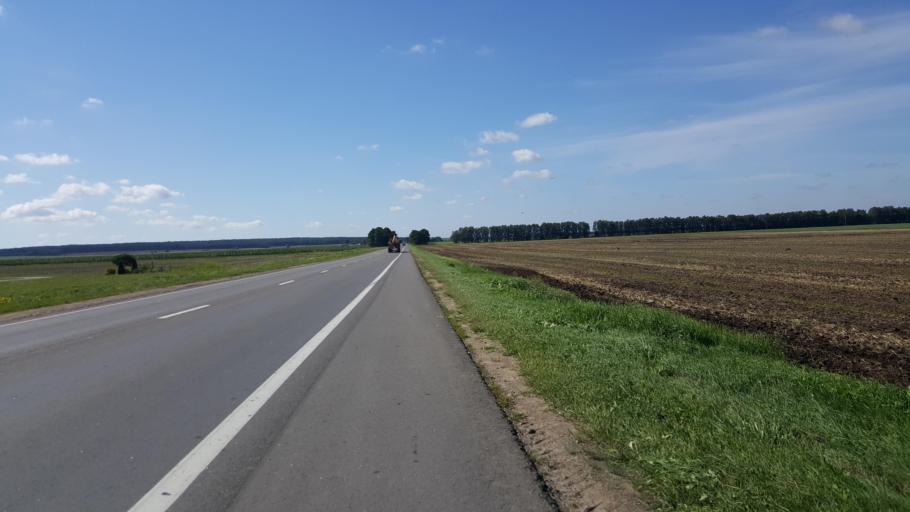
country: BY
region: Brest
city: Kamyanyets
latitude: 52.3226
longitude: 23.7825
